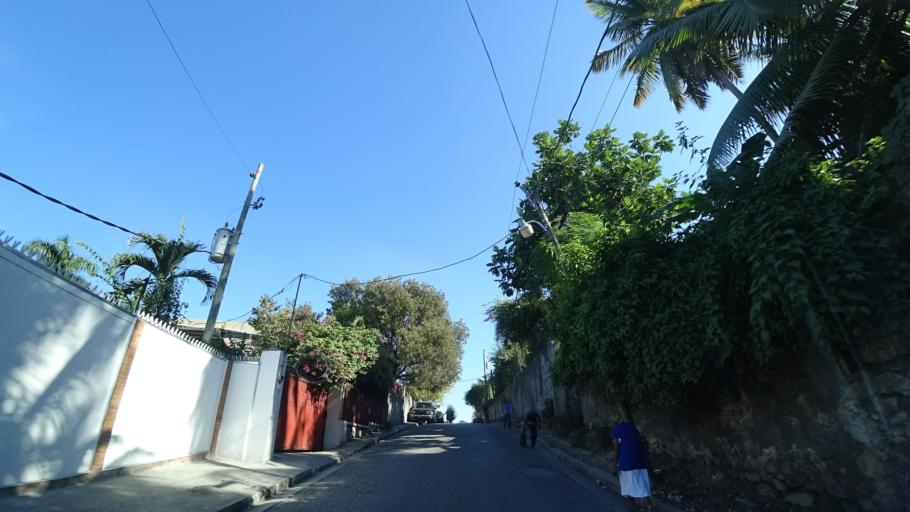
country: HT
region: Ouest
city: Port-au-Prince
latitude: 18.5315
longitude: -72.3209
